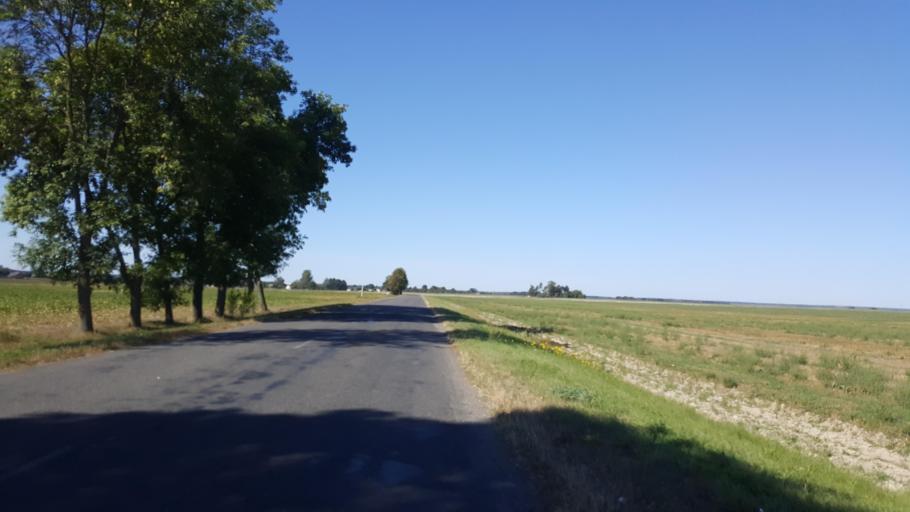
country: BY
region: Brest
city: Charnawchytsy
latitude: 52.2614
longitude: 23.5567
